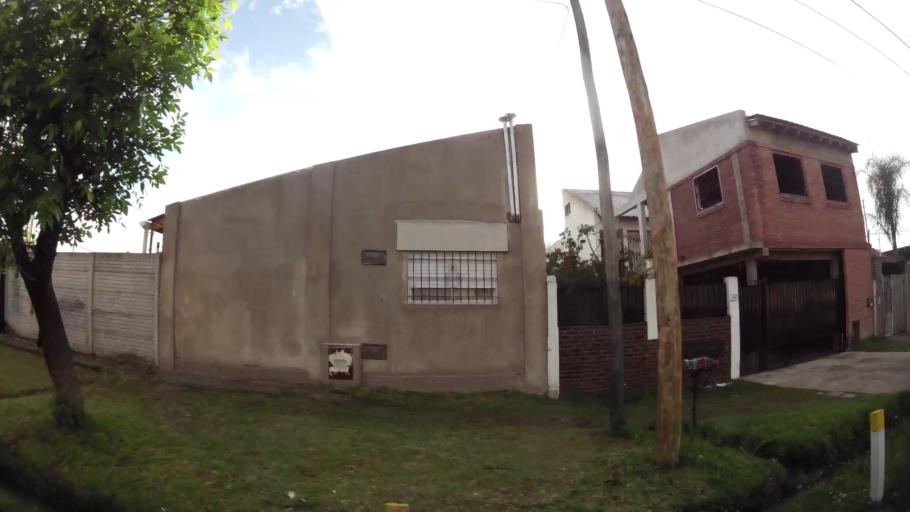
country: AR
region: Buenos Aires
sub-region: Partido de Almirante Brown
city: Adrogue
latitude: -34.7615
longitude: -58.3542
